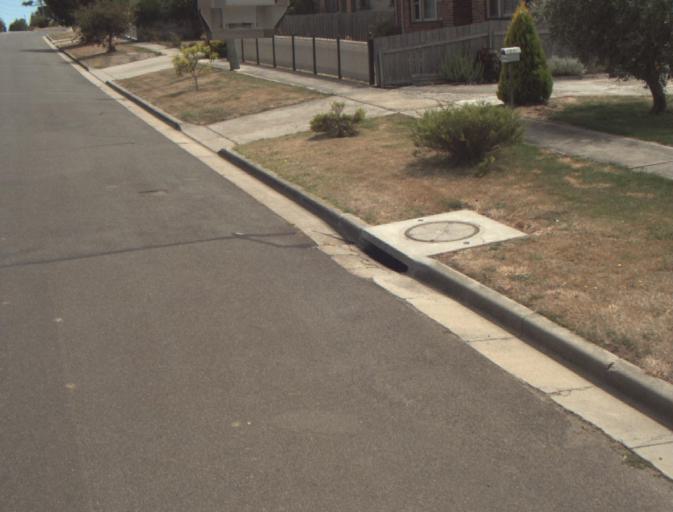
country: AU
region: Tasmania
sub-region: Launceston
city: Mayfield
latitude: -41.3836
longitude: 147.1113
